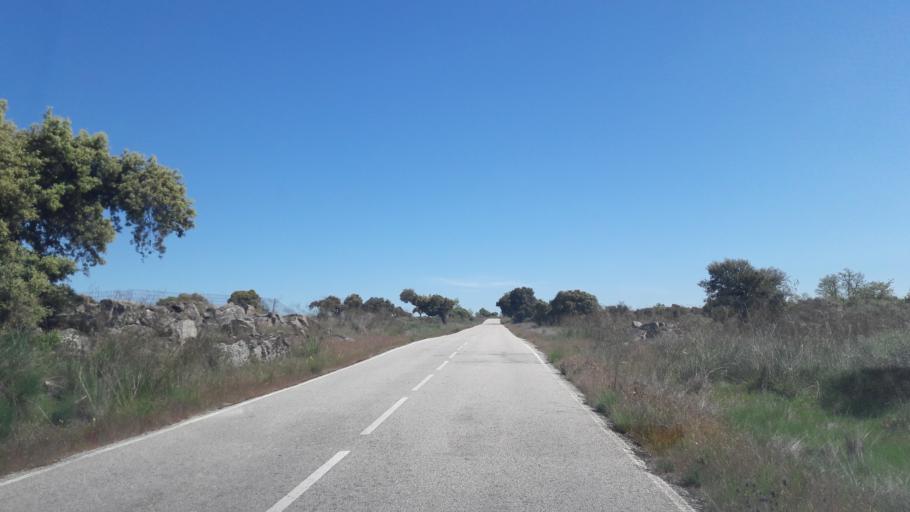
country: ES
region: Castille and Leon
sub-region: Provincia de Salamanca
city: Villarmuerto
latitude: 41.0391
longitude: -6.3927
